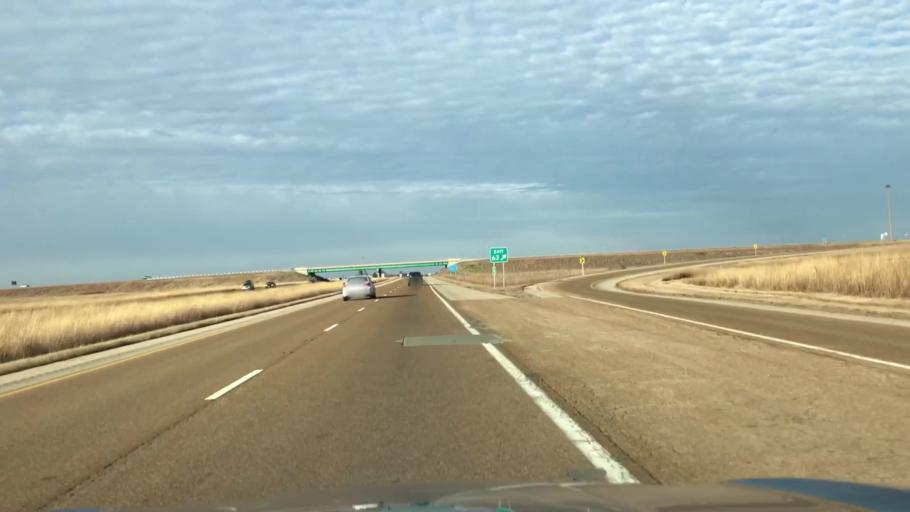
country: US
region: Illinois
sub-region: Montgomery County
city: Raymond
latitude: 39.3183
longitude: -89.6424
